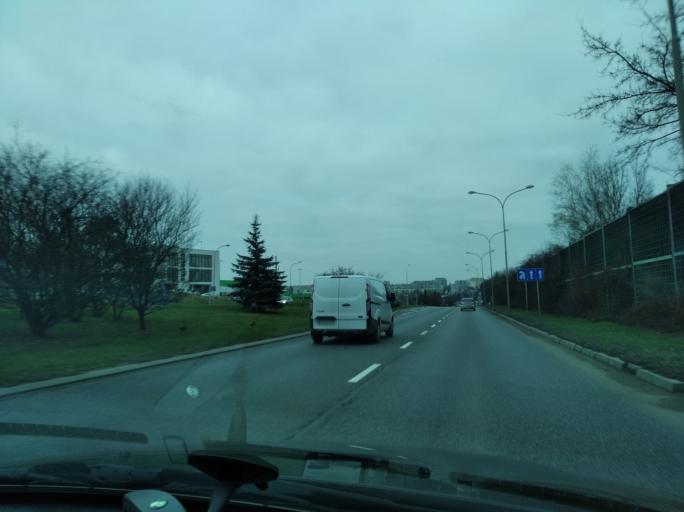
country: PL
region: Subcarpathian Voivodeship
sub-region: Rzeszow
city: Rzeszow
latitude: 50.0348
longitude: 21.9769
